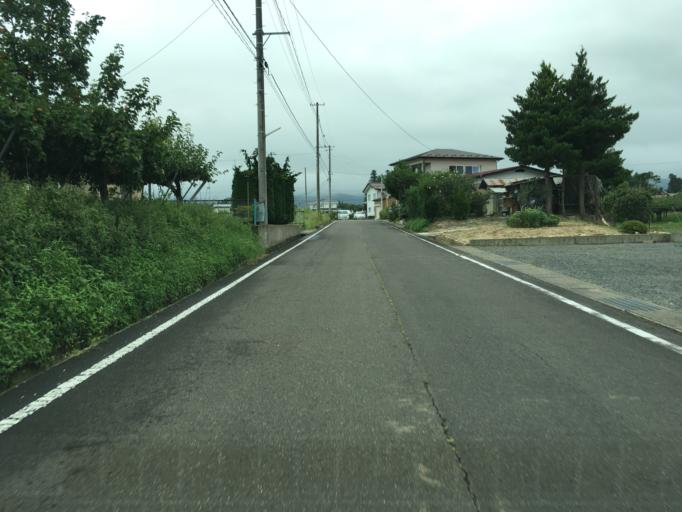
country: JP
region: Fukushima
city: Fukushima-shi
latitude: 37.7622
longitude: 140.3973
